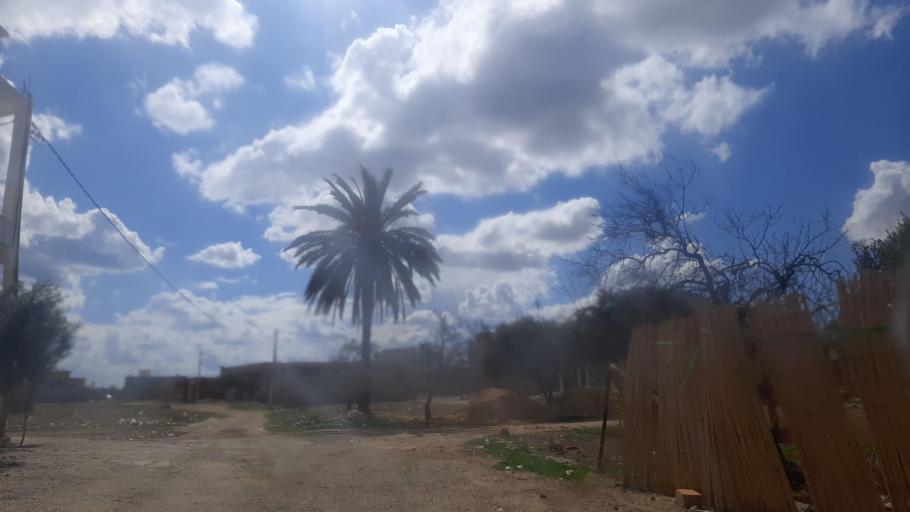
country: TN
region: Nabul
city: Korba
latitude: 36.5954
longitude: 10.8562
